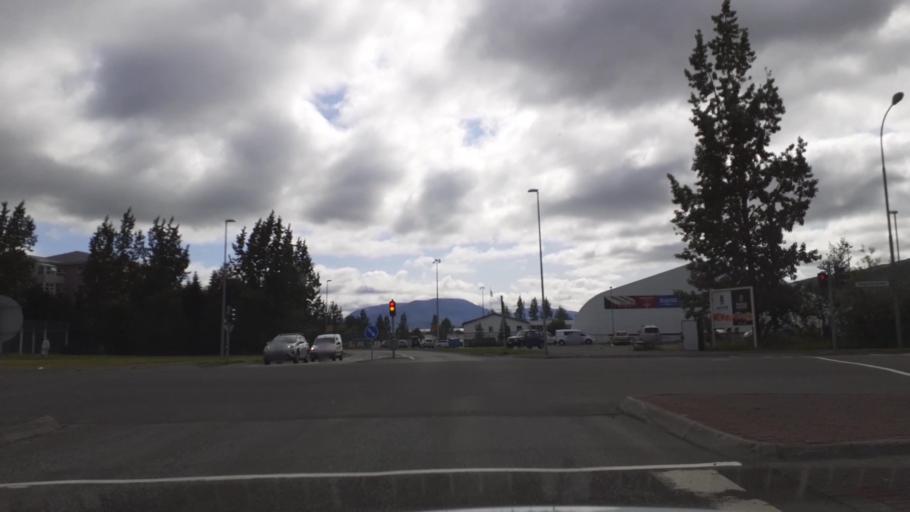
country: IS
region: Northeast
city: Akureyri
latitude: 65.6785
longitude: -18.1148
